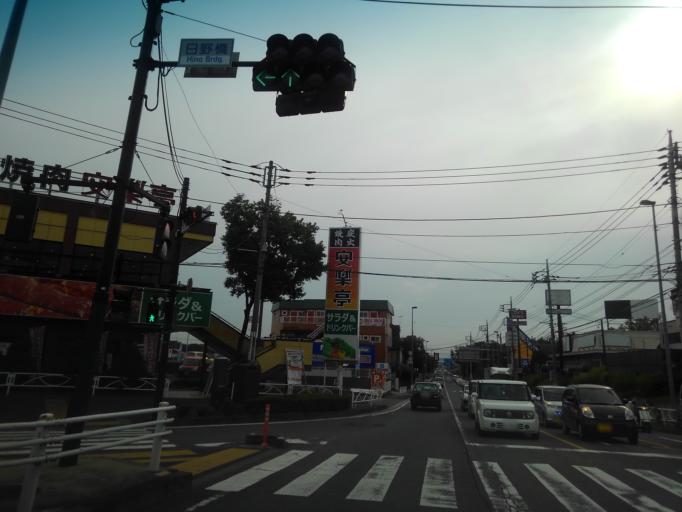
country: JP
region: Tokyo
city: Hino
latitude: 35.6867
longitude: 139.4149
